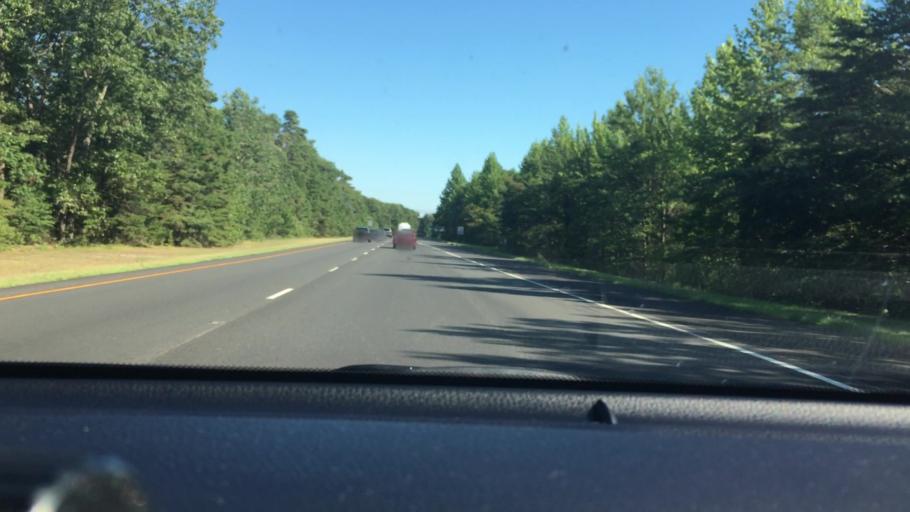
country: US
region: New Jersey
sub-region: Gloucester County
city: Clayton
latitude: 39.6323
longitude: -75.0944
